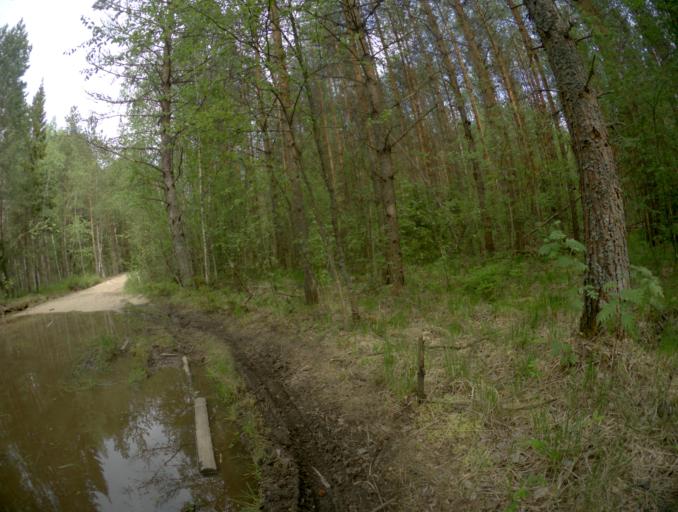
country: RU
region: Vladimir
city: Ivanishchi
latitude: 55.7495
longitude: 40.3801
